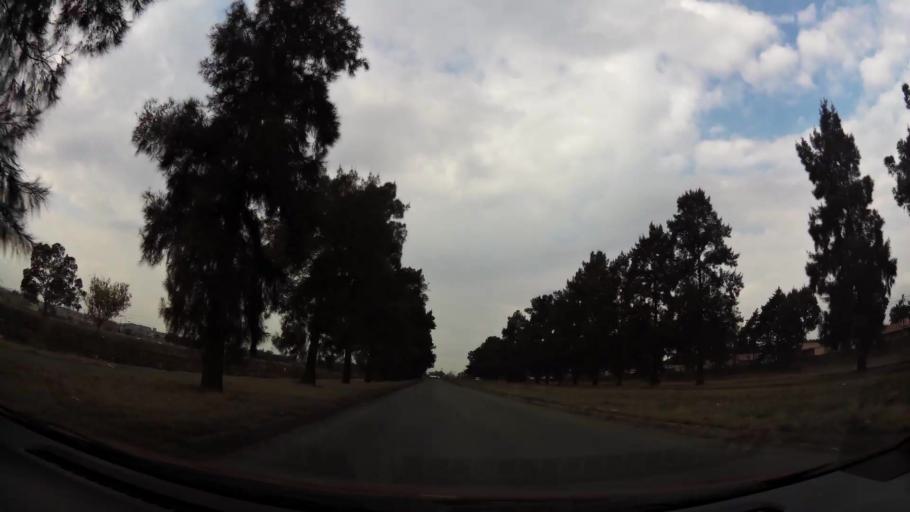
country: ZA
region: Gauteng
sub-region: Sedibeng District Municipality
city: Vanderbijlpark
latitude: -26.6739
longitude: 27.8335
